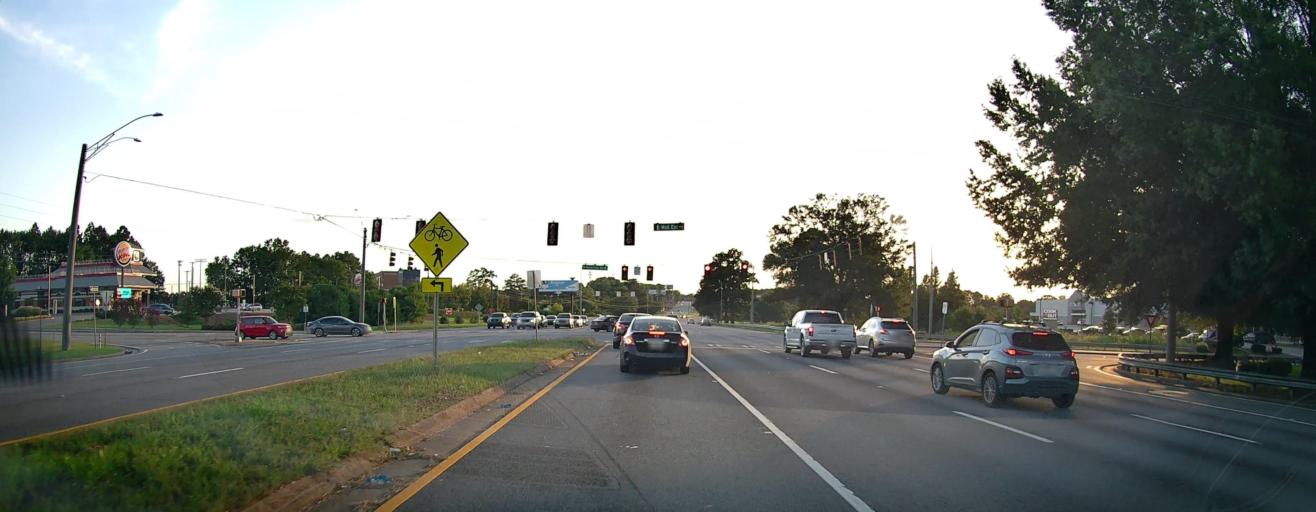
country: US
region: Georgia
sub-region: Muscogee County
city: Columbus
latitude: 32.5074
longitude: -84.9397
